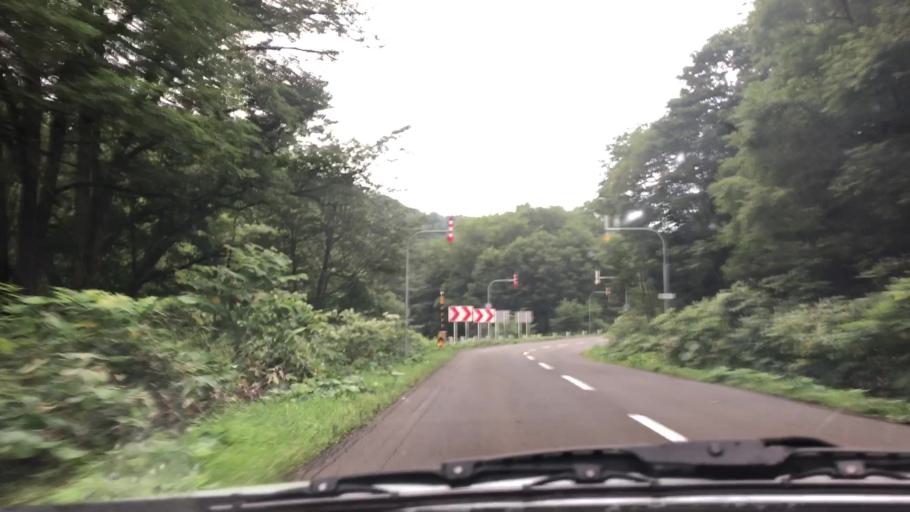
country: JP
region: Hokkaido
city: Shimo-furano
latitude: 42.9210
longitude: 142.3747
